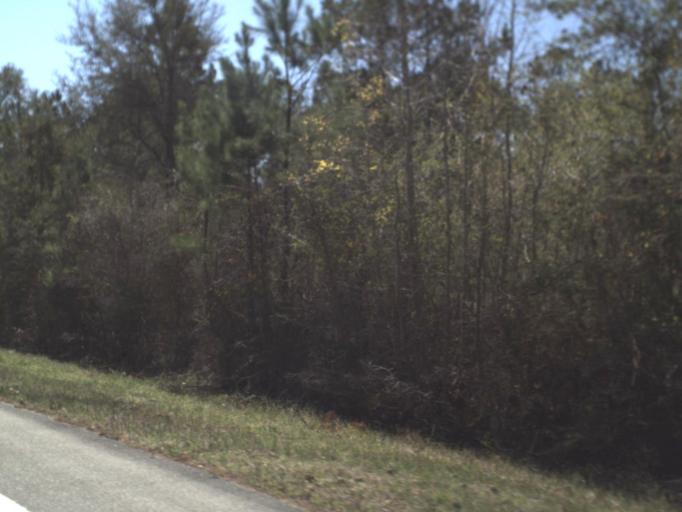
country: US
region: Florida
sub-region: Leon County
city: Woodville
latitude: 30.2168
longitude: -84.2246
